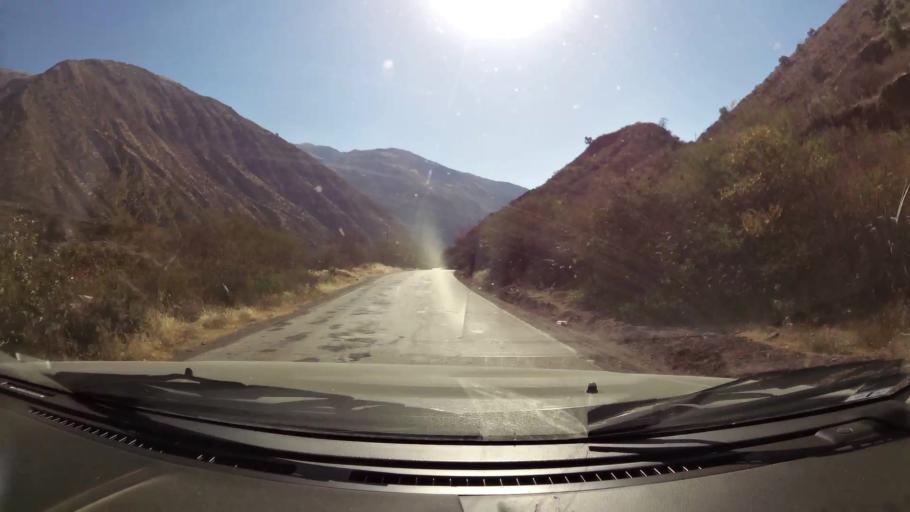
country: PE
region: Huancavelica
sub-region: Provincia de Acobamba
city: Pomacocha
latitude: -12.7627
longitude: -74.5202
